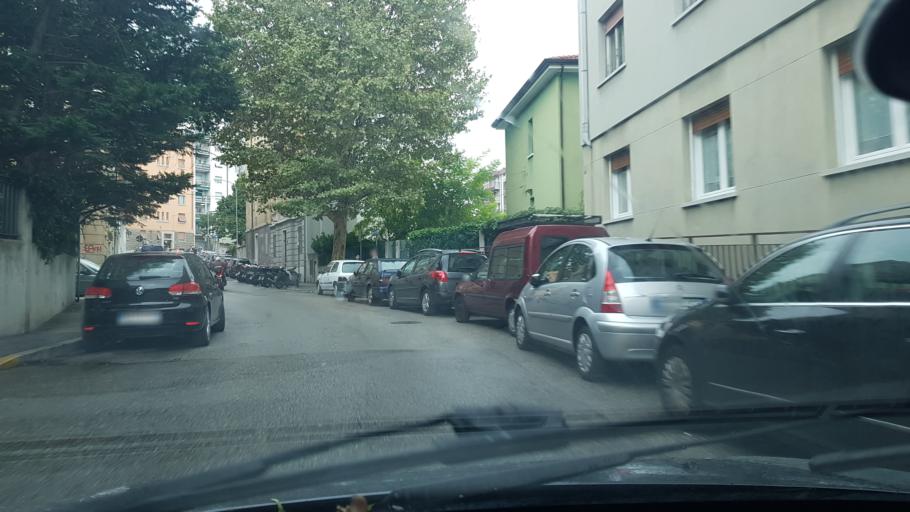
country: IT
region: Friuli Venezia Giulia
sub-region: Provincia di Trieste
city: Trieste
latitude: 45.6416
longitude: 13.7799
